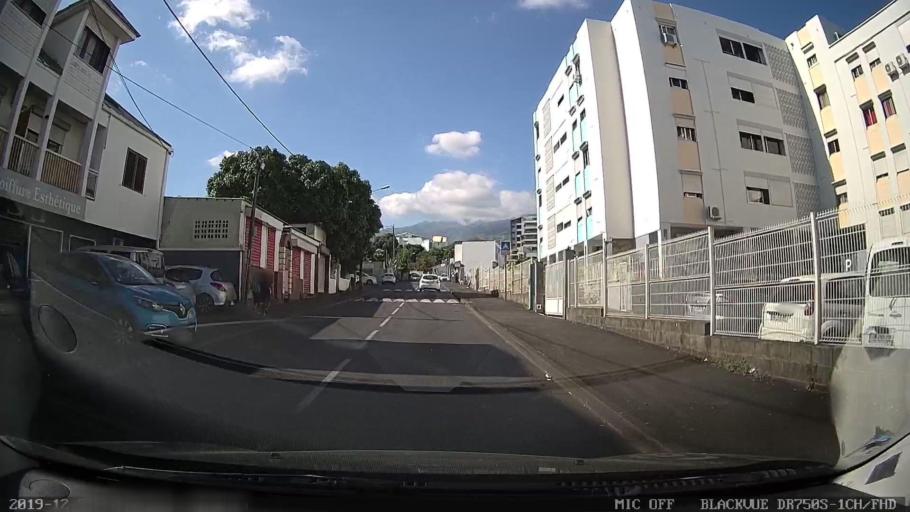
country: RE
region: Reunion
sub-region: Reunion
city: Saint-Denis
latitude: -20.8935
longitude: 55.4818
